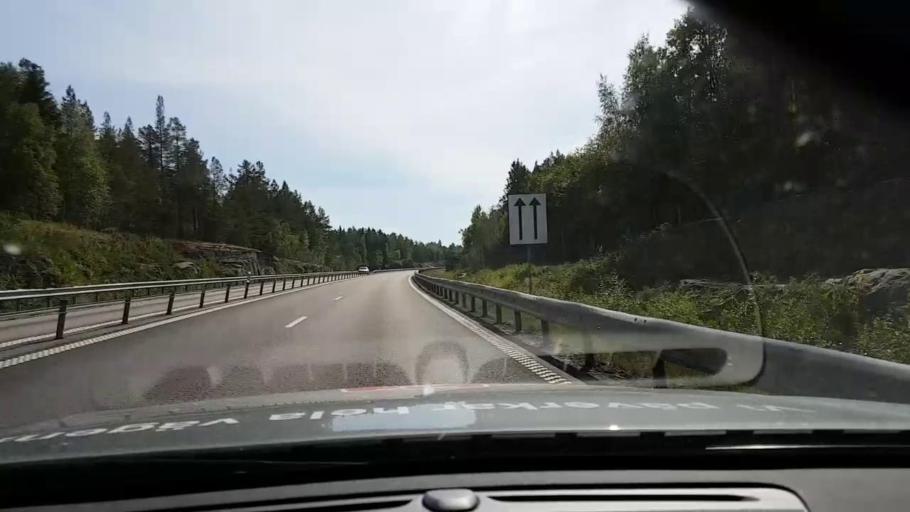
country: SE
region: Vaesternorrland
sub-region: OErnskoeldsviks Kommun
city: Husum
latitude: 63.3889
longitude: 19.1944
